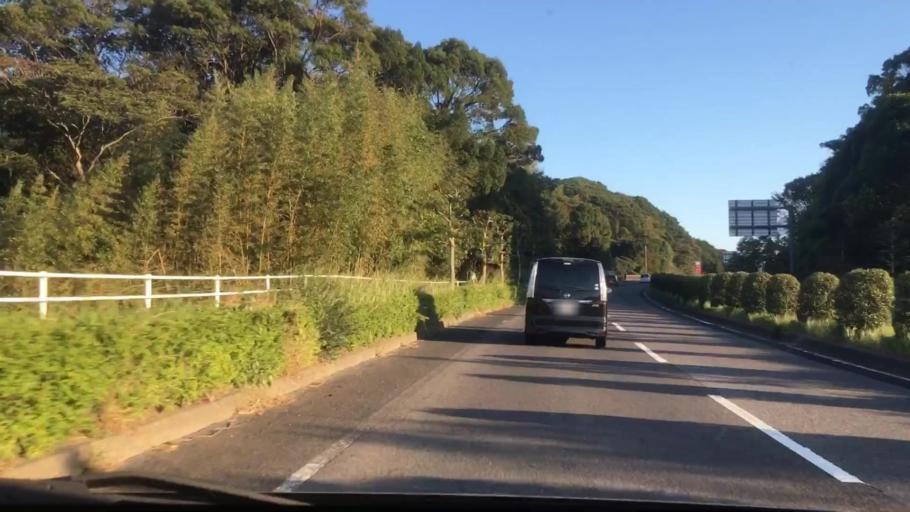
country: JP
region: Nagasaki
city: Sasebo
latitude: 33.1397
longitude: 129.7845
